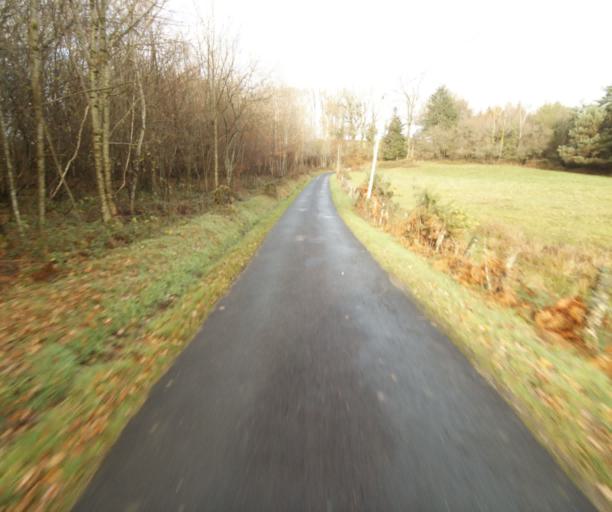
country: FR
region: Limousin
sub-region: Departement de la Correze
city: Saint-Mexant
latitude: 45.2584
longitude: 1.6399
